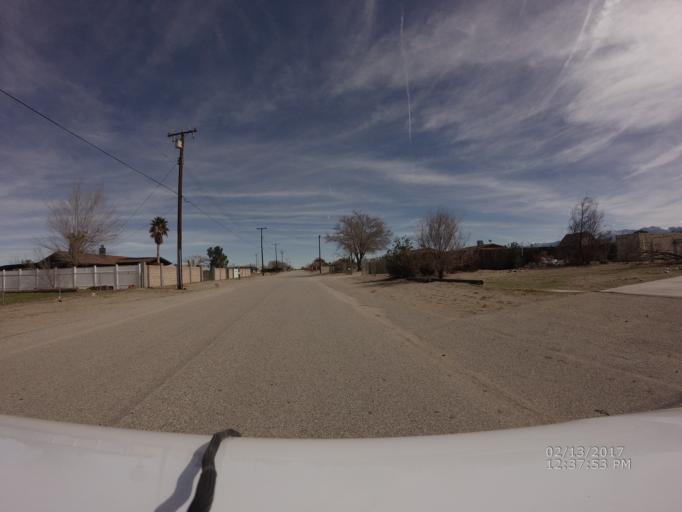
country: US
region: California
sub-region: Los Angeles County
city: Littlerock
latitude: 34.5707
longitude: -117.9266
